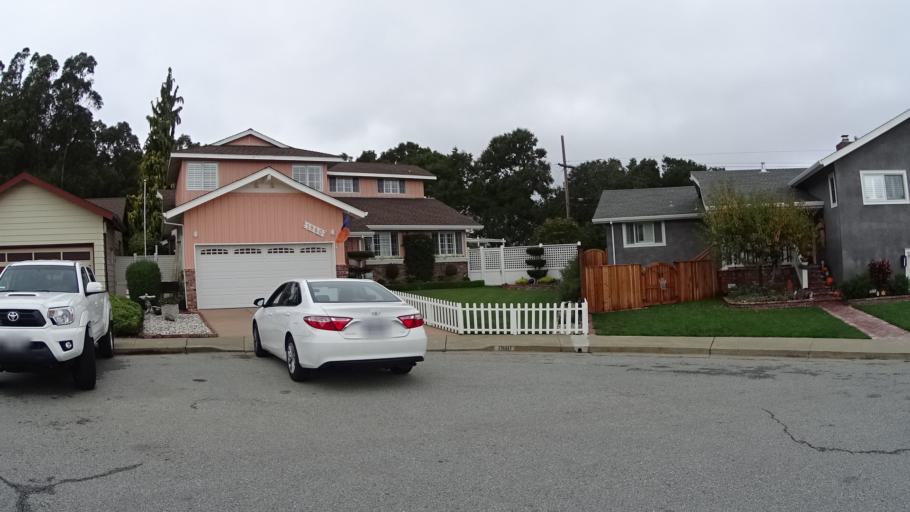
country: US
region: California
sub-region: San Mateo County
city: San Bruno
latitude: 37.6124
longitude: -122.4190
